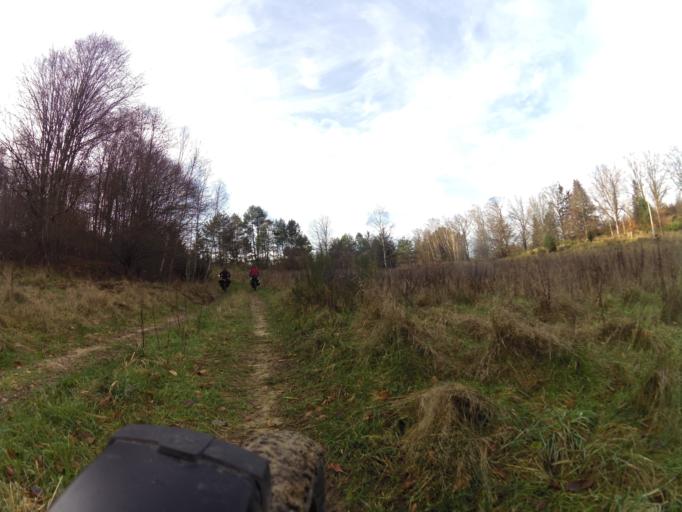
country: PL
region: West Pomeranian Voivodeship
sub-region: Powiat koszalinski
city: Polanow
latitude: 54.0790
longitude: 16.6618
